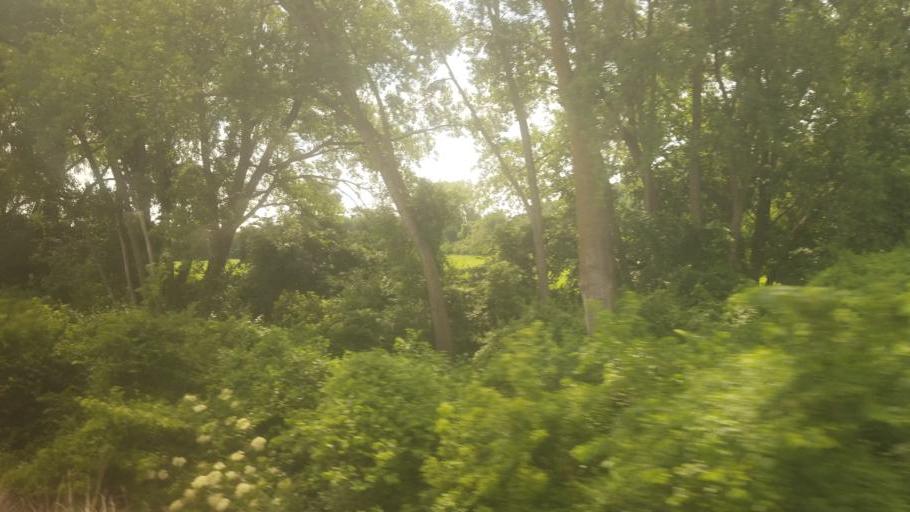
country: US
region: Missouri
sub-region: Jackson County
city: East Independence
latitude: 39.1732
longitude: -94.3392
